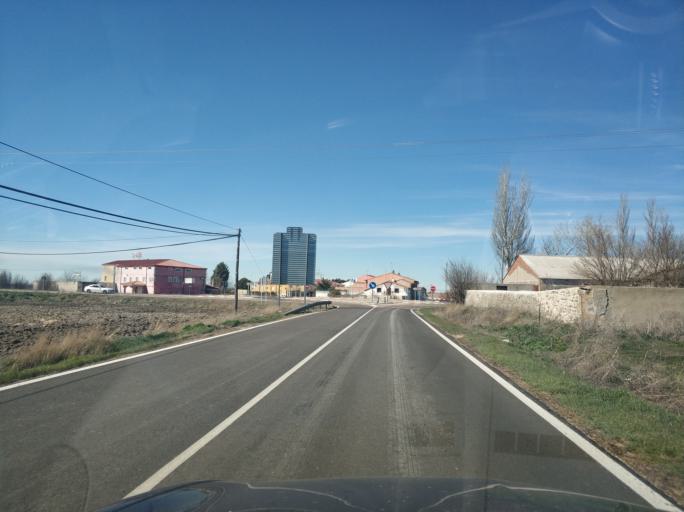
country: ES
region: Castille and Leon
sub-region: Provincia de Salamanca
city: Pedrosillo el Ralo
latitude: 41.0596
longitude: -5.5471
